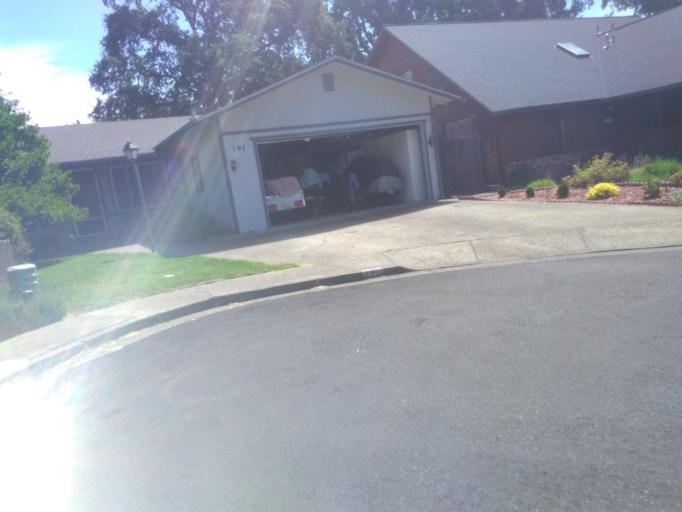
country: US
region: California
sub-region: Mendocino County
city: Ukiah
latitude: 39.1469
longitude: -123.2186
